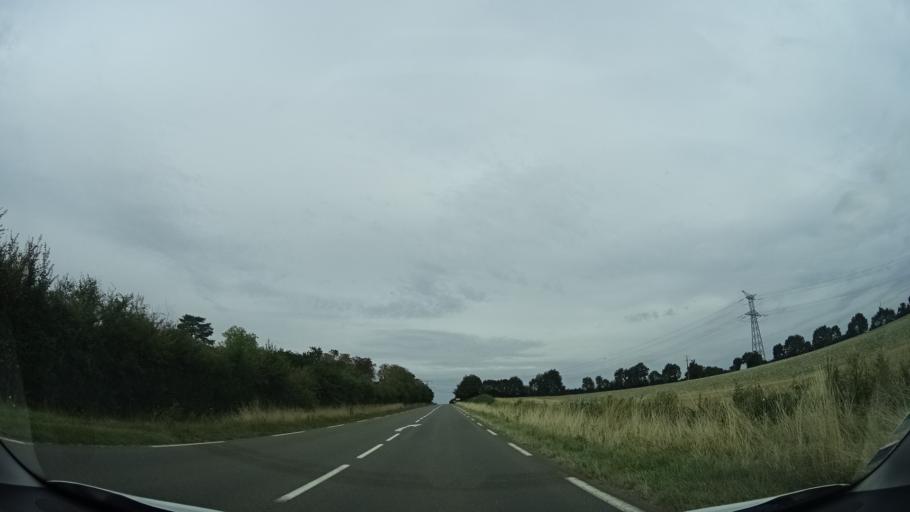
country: FR
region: Pays de la Loire
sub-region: Departement de la Sarthe
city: Auvers-le-Hamon
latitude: 47.8972
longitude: -0.4320
